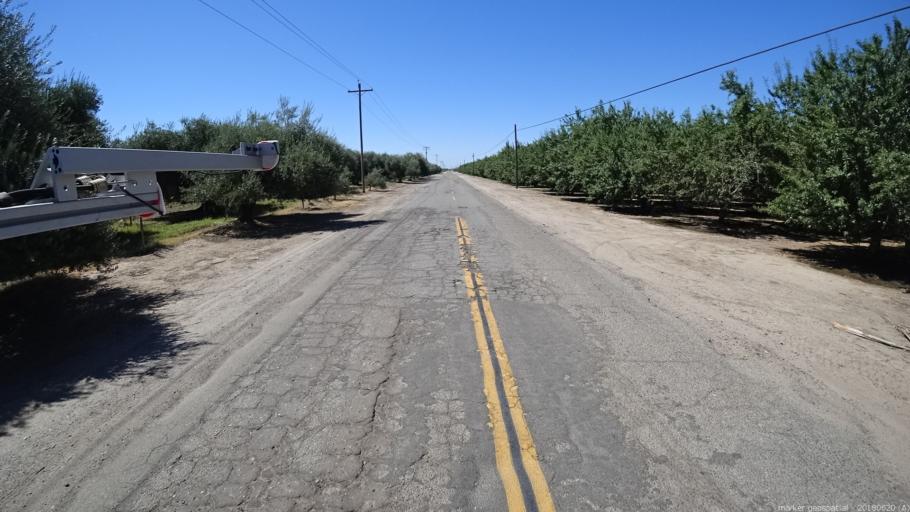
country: US
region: California
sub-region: Madera County
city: Parkwood
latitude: 36.9088
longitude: -120.0104
